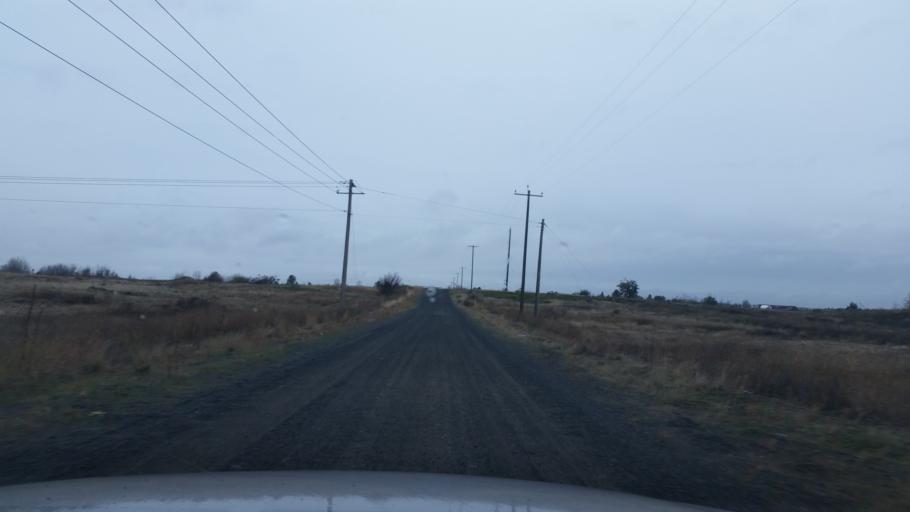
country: US
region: Washington
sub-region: Spokane County
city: Airway Heights
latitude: 47.6284
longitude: -117.6071
